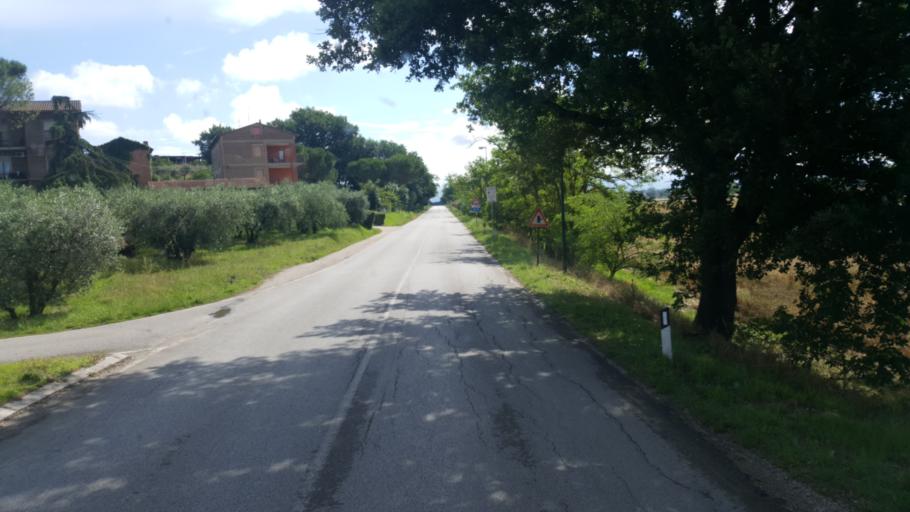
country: IT
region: Umbria
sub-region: Provincia di Perugia
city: Torgiano
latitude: 43.0346
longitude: 12.4452
